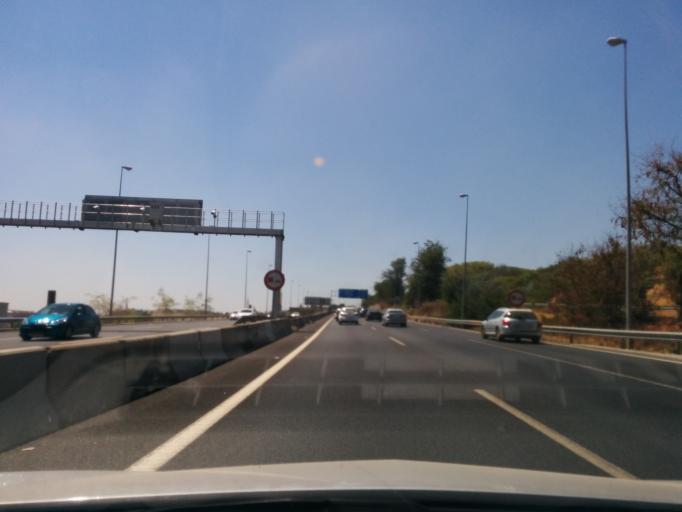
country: ES
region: Andalusia
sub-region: Provincia de Sevilla
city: Camas
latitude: 37.3879
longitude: -6.0340
